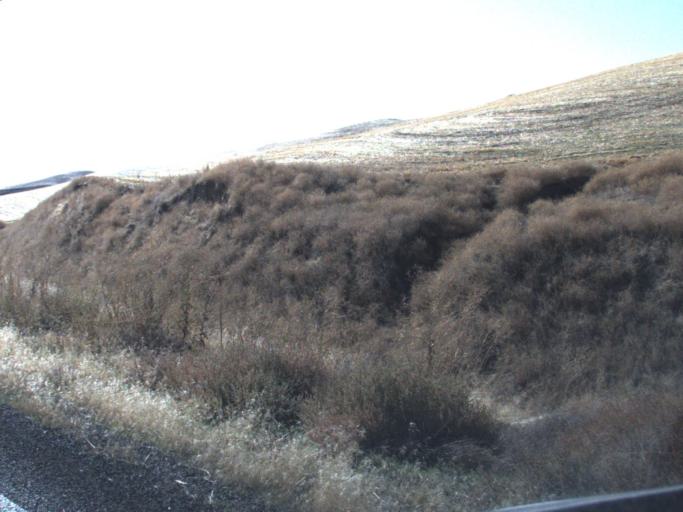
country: US
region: Washington
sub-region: Walla Walla County
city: Waitsburg
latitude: 46.2656
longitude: -118.3514
